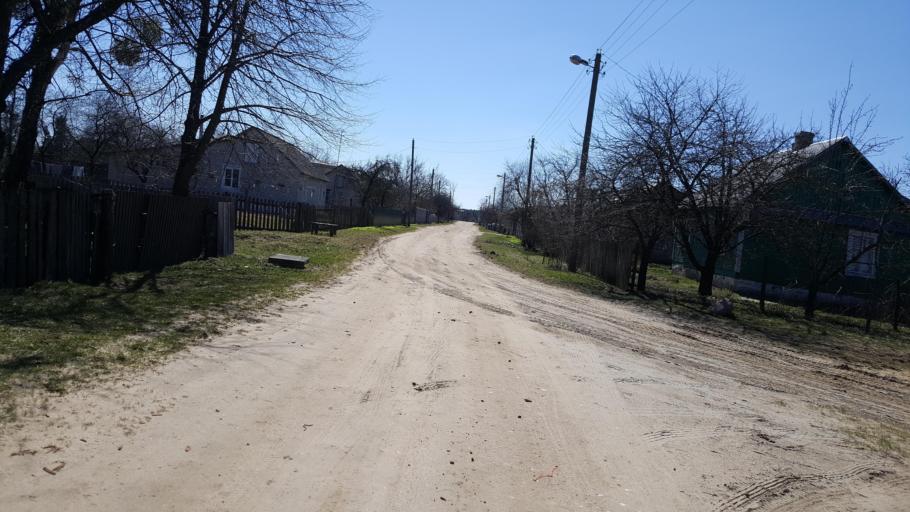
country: BY
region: Brest
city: Kamyanyets
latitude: 52.2936
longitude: 23.8564
